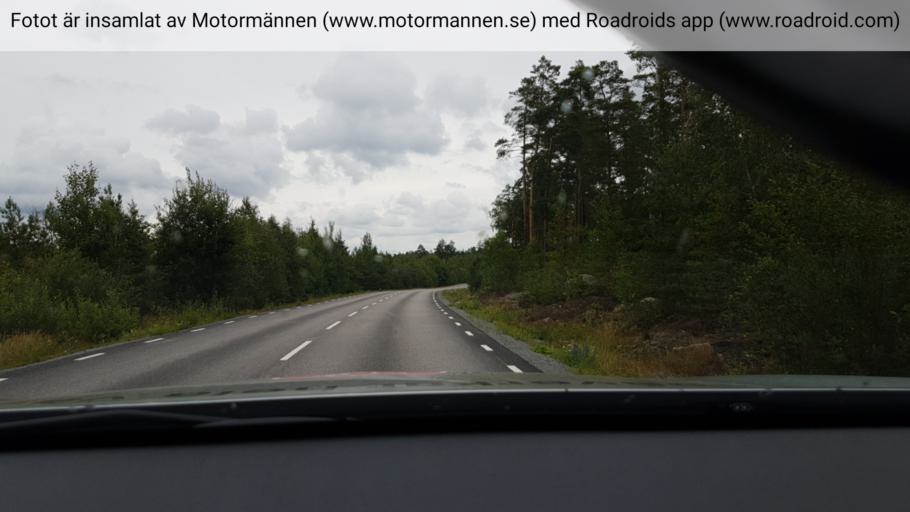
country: SE
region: Stockholm
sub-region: Sigtuna Kommun
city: Rosersberg
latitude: 59.6186
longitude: 17.9116
